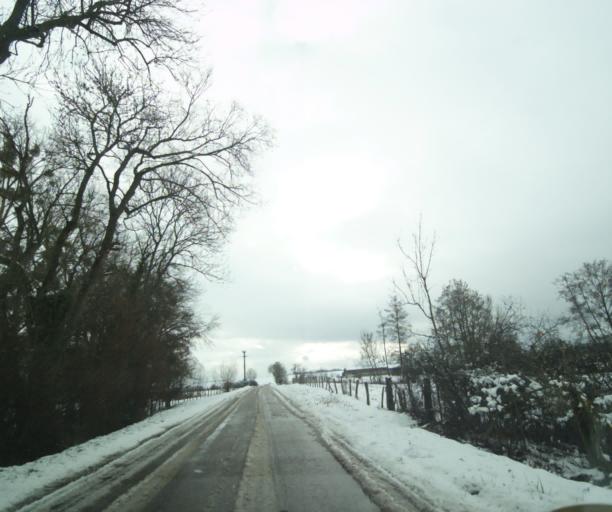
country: FR
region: Champagne-Ardenne
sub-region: Departement de la Haute-Marne
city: Montier-en-Der
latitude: 48.4522
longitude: 4.6952
